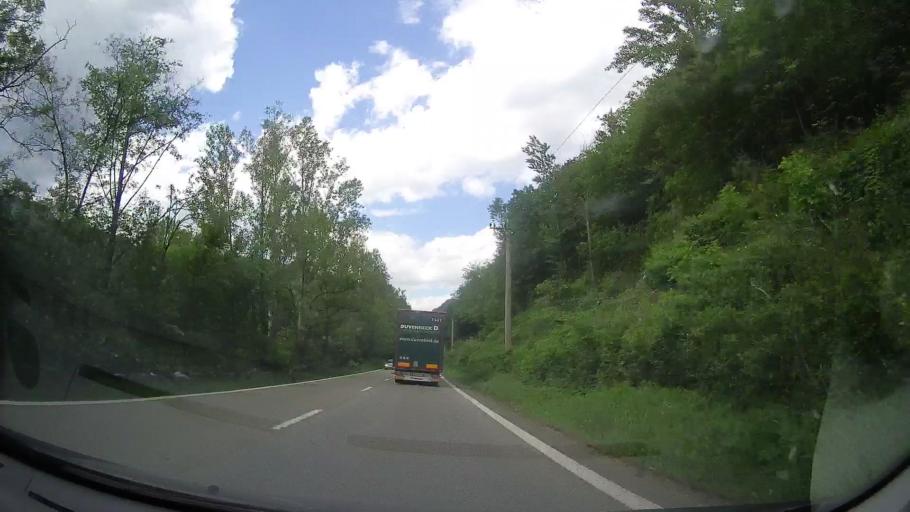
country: RO
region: Valcea
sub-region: Oras Calimanesti
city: Calimanesti
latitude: 45.2719
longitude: 24.3187
